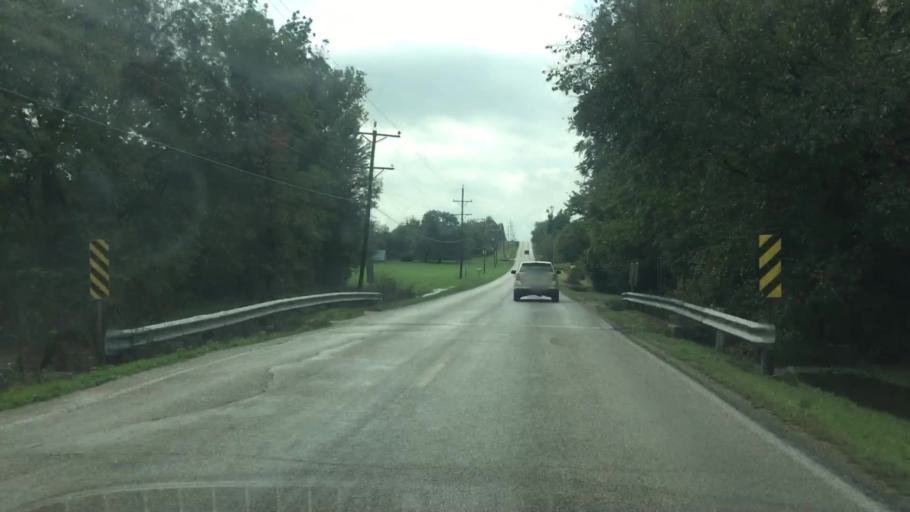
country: US
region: Kansas
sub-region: Allen County
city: Humboldt
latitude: 37.8666
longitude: -95.4369
